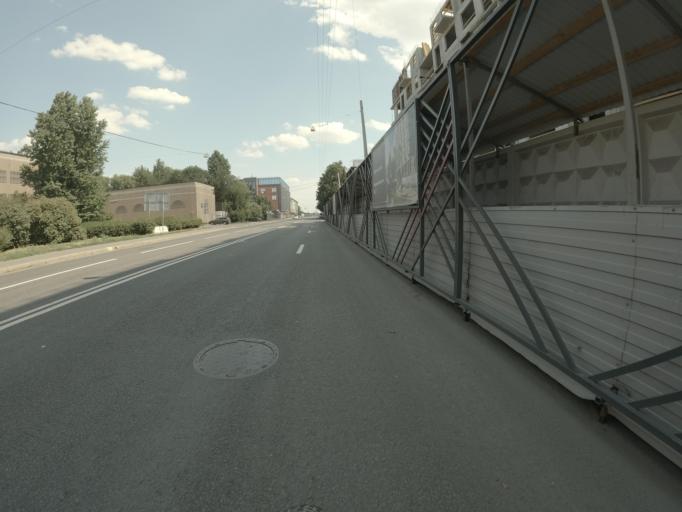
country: RU
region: St.-Petersburg
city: Vasyl'evsky Ostrov
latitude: 59.9091
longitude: 30.2525
